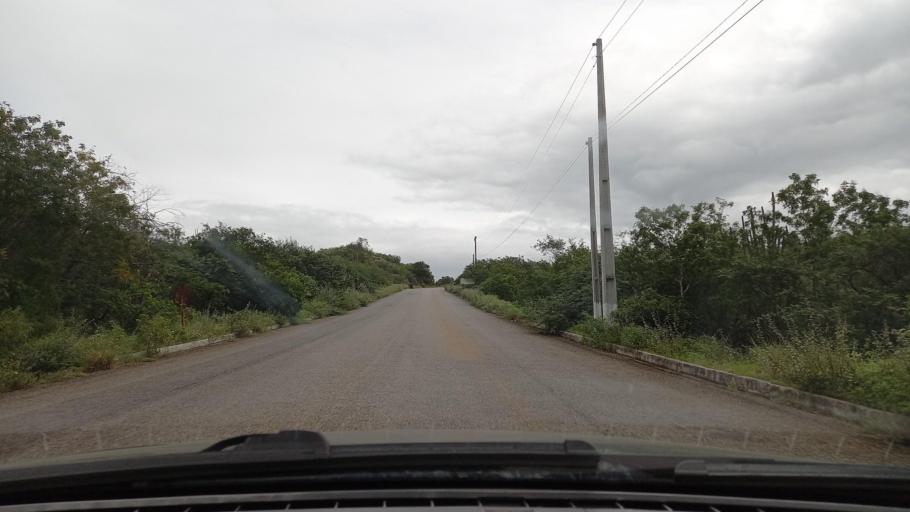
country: BR
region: Sergipe
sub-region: Caninde De Sao Francisco
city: Caninde de Sao Francisco
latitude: -9.6320
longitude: -37.7825
